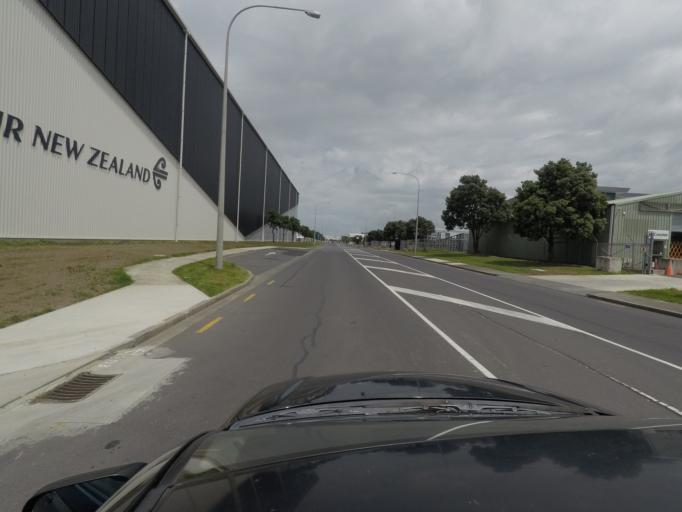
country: NZ
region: Auckland
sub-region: Auckland
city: Mangere
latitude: -37.0013
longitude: 174.7981
